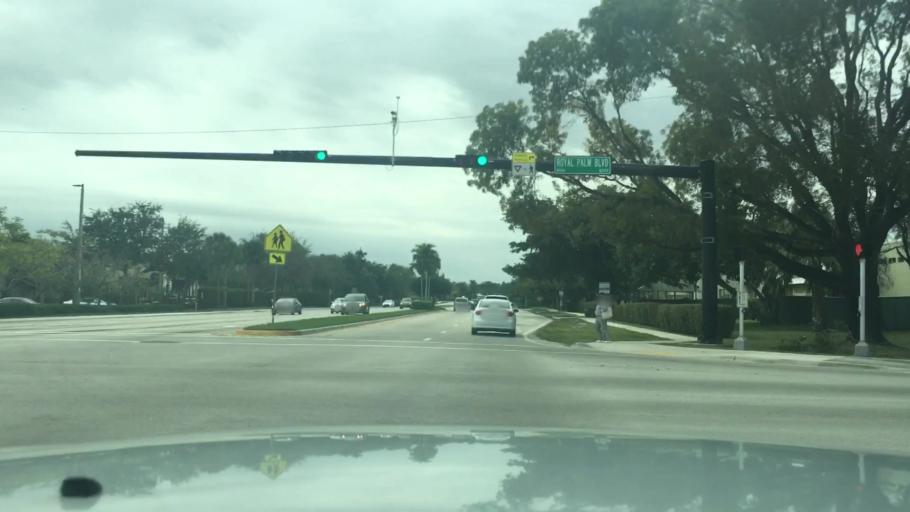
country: US
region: Florida
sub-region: Broward County
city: Margate
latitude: 26.2579
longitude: -80.2366
